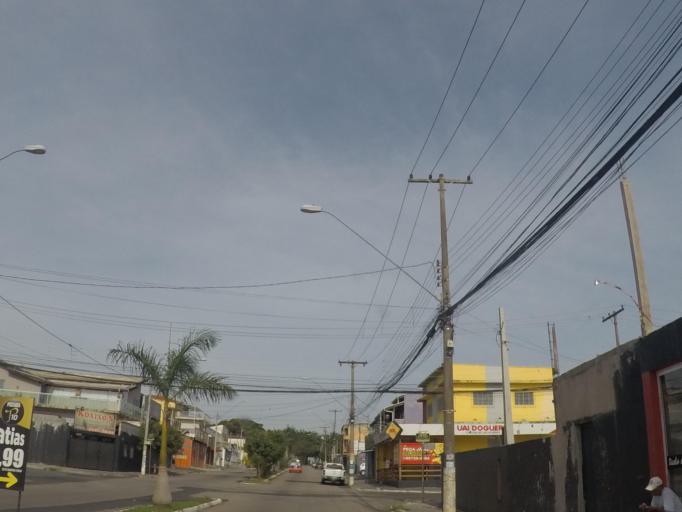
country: BR
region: Sao Paulo
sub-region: Hortolandia
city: Hortolandia
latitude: -22.8536
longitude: -47.1860
